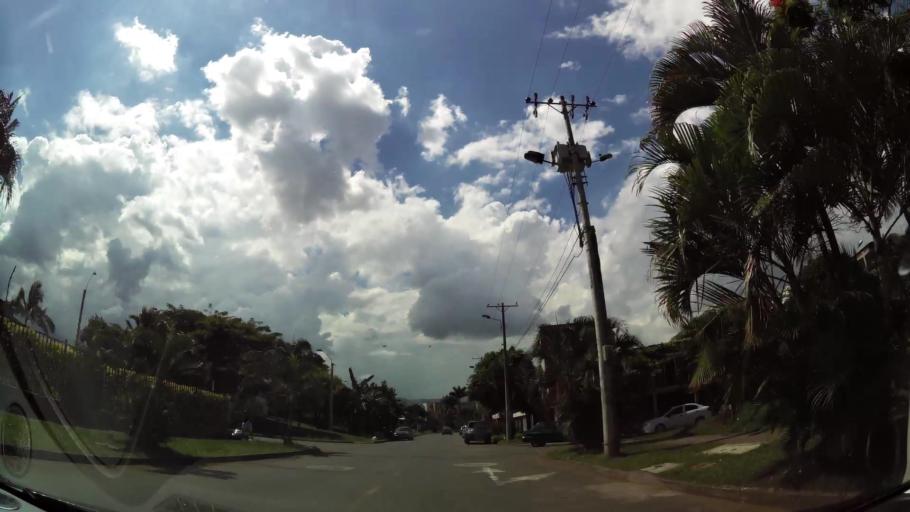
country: CO
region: Valle del Cauca
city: Cali
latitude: 3.3937
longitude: -76.5183
